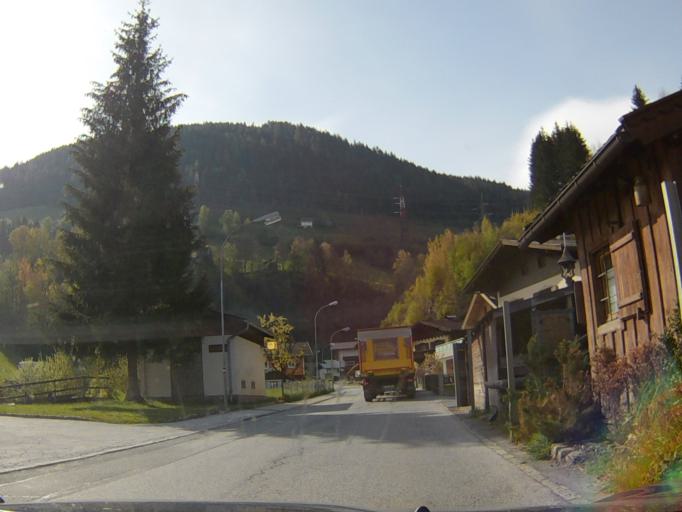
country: AT
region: Salzburg
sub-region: Politischer Bezirk Zell am See
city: Mittersill
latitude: 47.2748
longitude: 12.4846
